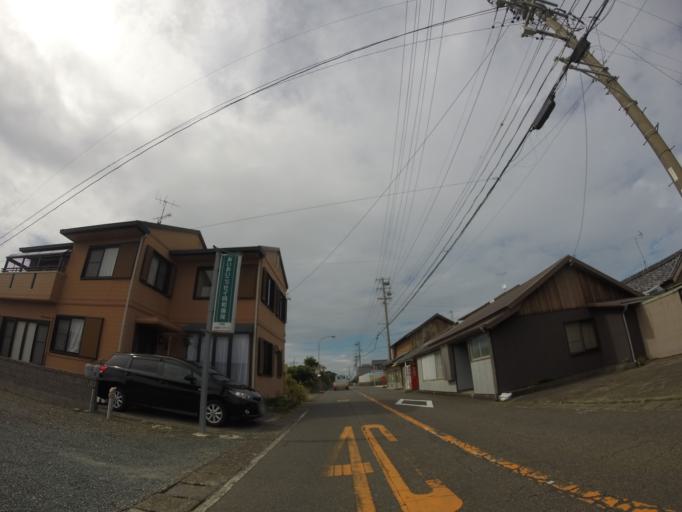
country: JP
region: Shizuoka
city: Oyama
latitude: 34.6230
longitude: 138.2006
